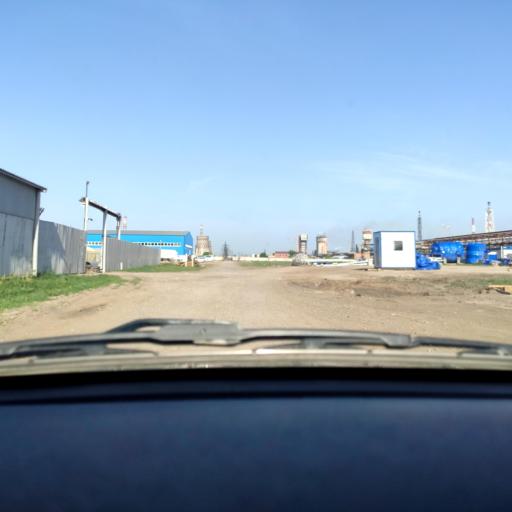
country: RU
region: Samara
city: Tol'yatti
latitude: 53.5450
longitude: 49.4808
